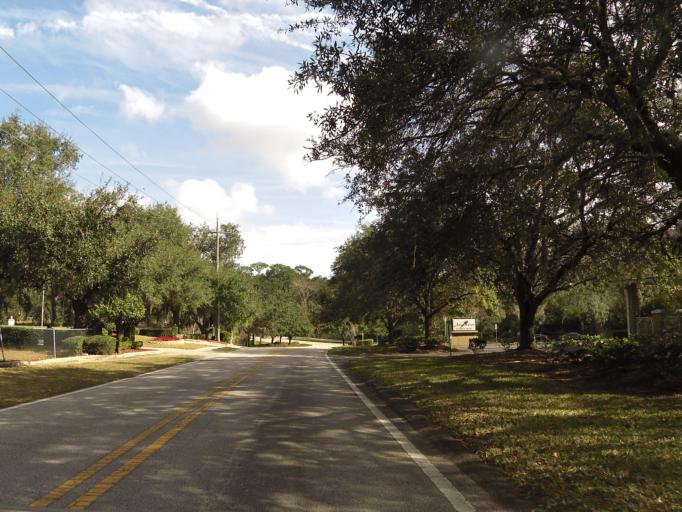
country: US
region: Florida
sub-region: Duval County
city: Jacksonville
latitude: 30.3329
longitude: -81.5857
